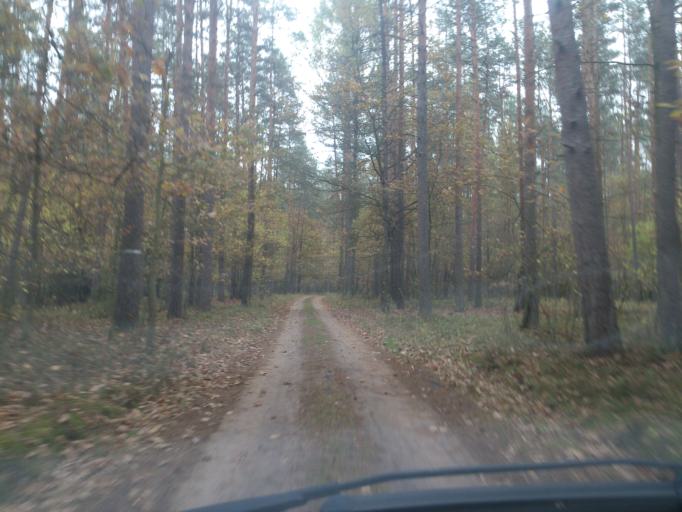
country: PL
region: Kujawsko-Pomorskie
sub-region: Powiat golubsko-dobrzynski
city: Golub-Dobrzyn
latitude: 53.1356
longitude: 19.1204
